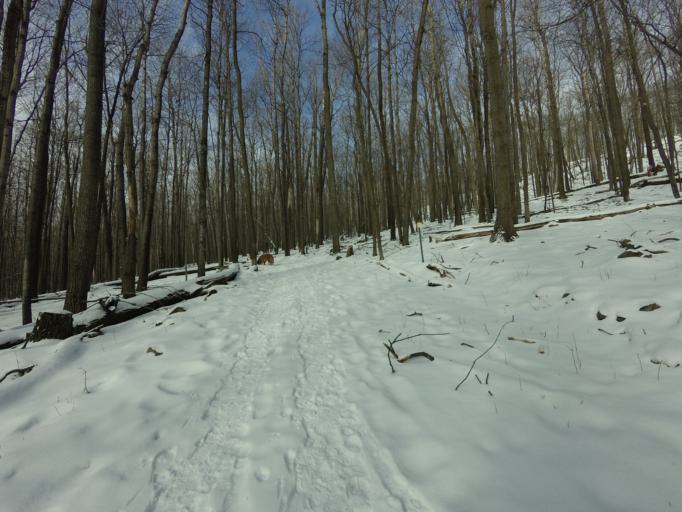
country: US
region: Wisconsin
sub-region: Marathon County
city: Rib Mountain
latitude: 44.9170
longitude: -89.6755
